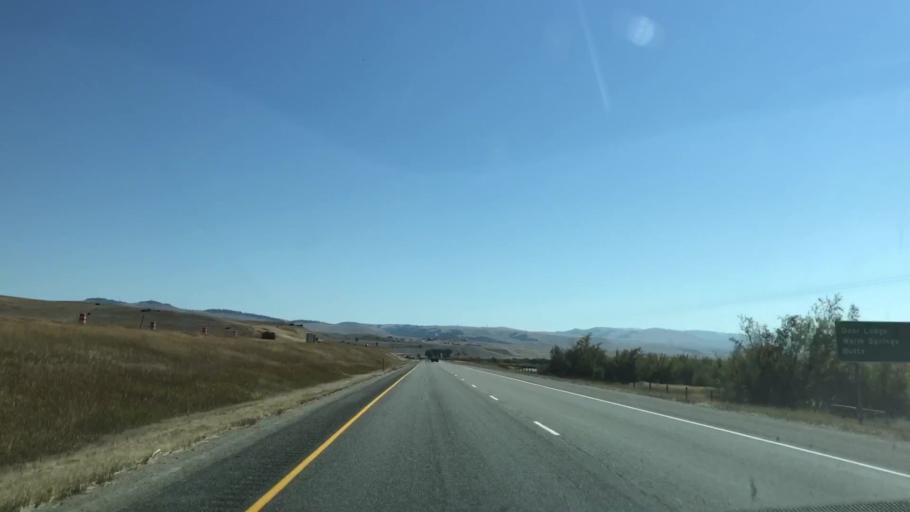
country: US
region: Montana
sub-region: Powell County
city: Deer Lodge
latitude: 46.5054
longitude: -112.7702
